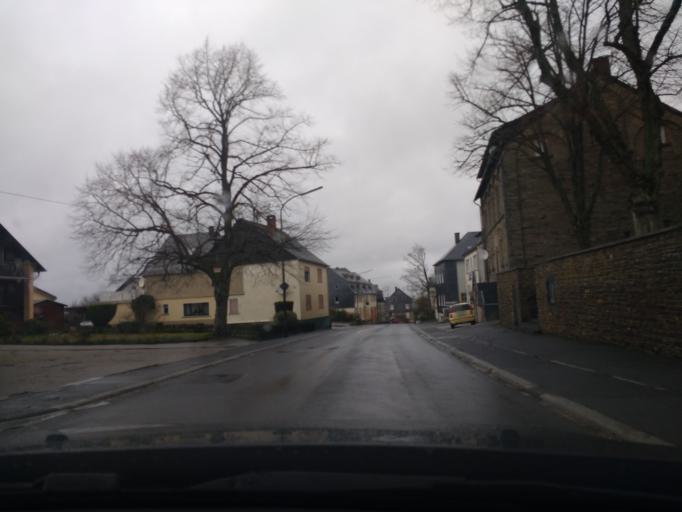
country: DE
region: Rheinland-Pfalz
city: Irmenach
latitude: 49.9228
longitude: 7.1889
